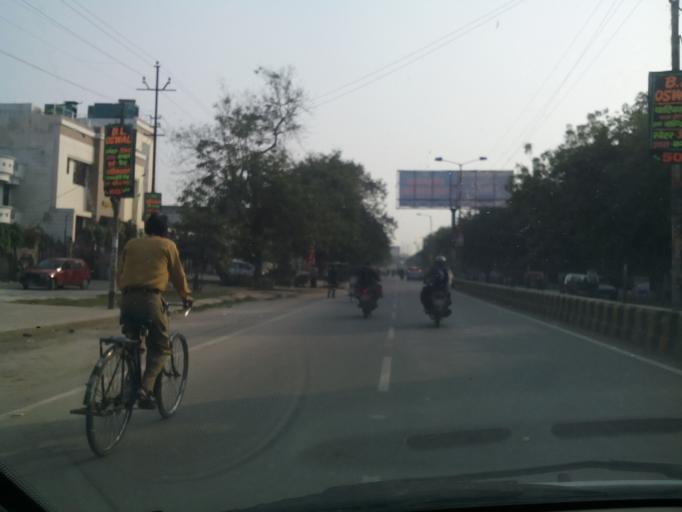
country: IN
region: Uttar Pradesh
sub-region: Kanpur
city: Kanpur
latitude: 26.4379
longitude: 80.3088
